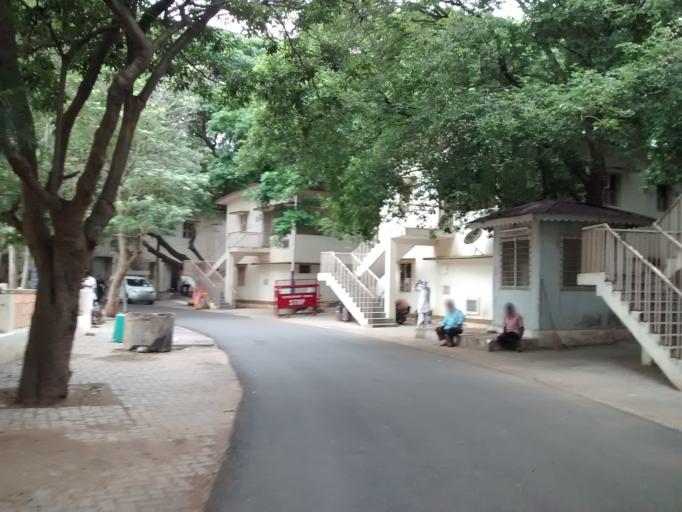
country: IN
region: Andhra Pradesh
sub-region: Chittoor
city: Tirumala
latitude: 13.6794
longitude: 79.3491
